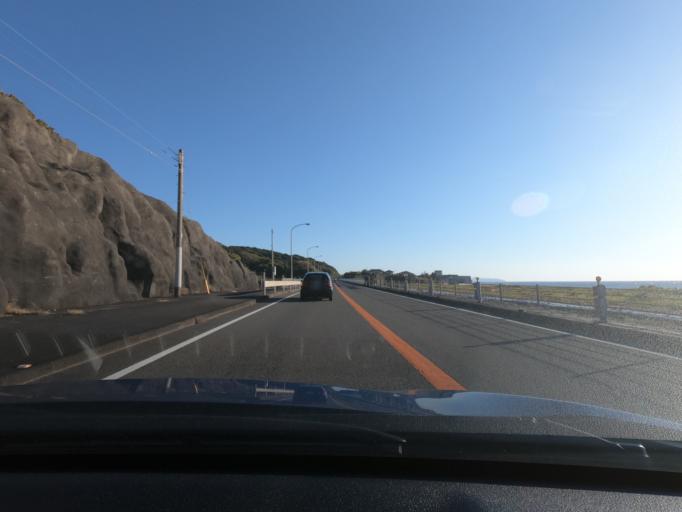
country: JP
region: Kagoshima
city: Akune
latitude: 31.9431
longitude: 130.2166
